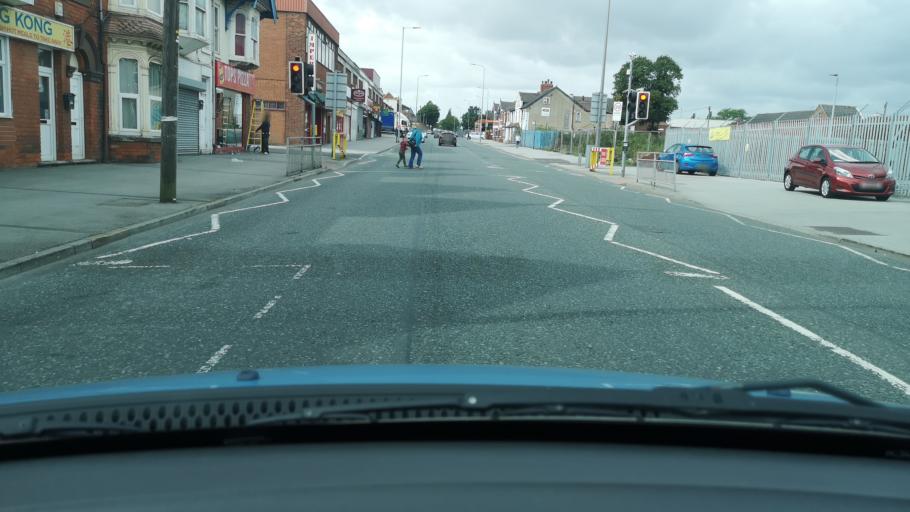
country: GB
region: England
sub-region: North Lincolnshire
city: Scunthorpe
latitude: 53.5909
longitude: -0.6558
